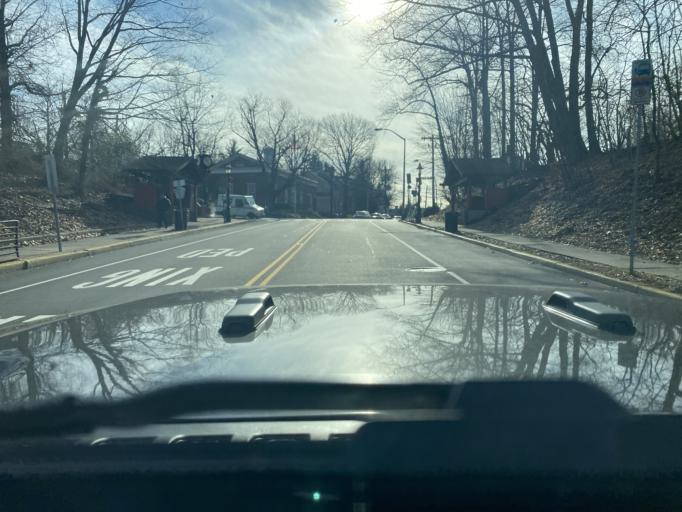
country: US
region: New Jersey
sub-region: Middlesex County
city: Metuchen
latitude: 40.5406
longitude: -74.3608
